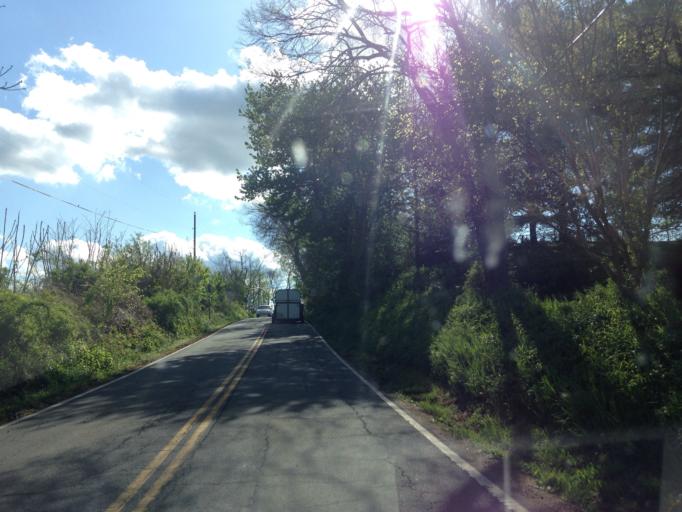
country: US
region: Virginia
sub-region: Loudoun County
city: Lovettsville
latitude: 39.2698
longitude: -77.6315
